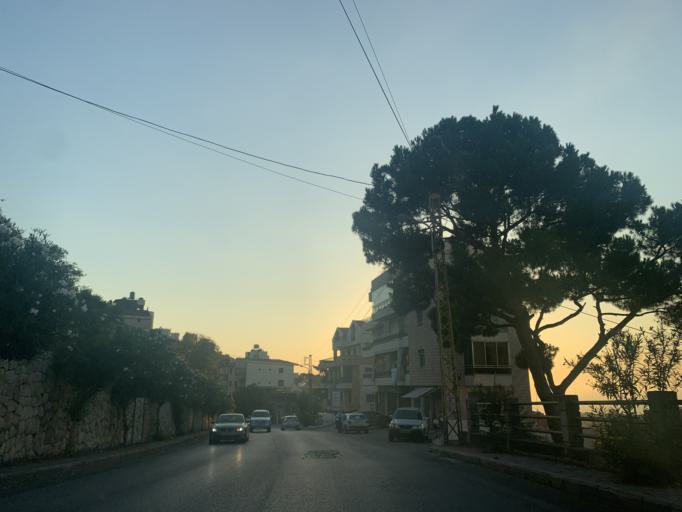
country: LB
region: Mont-Liban
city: Djounie
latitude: 33.9565
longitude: 35.6434
